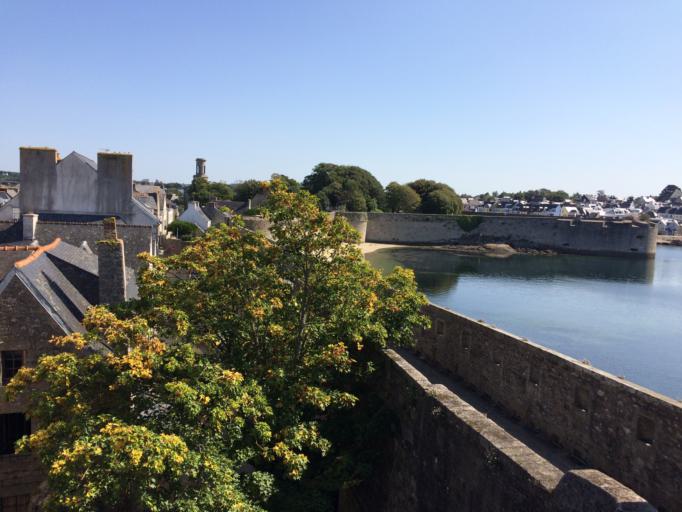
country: FR
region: Brittany
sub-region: Departement du Finistere
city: Concarneau
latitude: 47.8717
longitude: -3.9159
